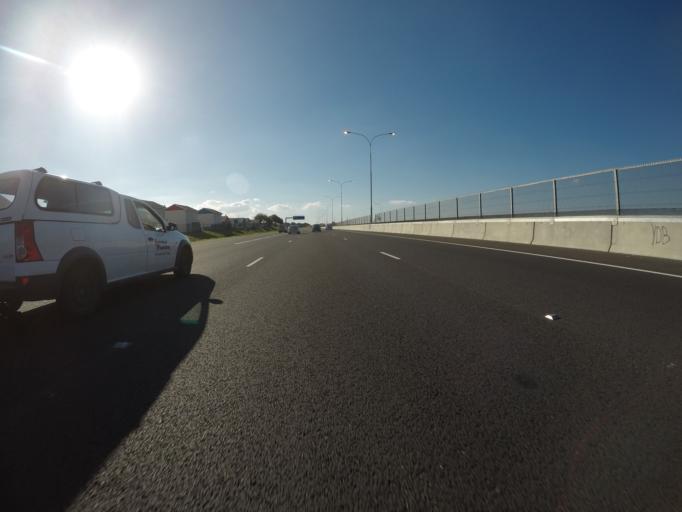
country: ZA
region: Western Cape
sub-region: City of Cape Town
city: Kraaifontein
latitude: -33.9616
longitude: 18.6558
